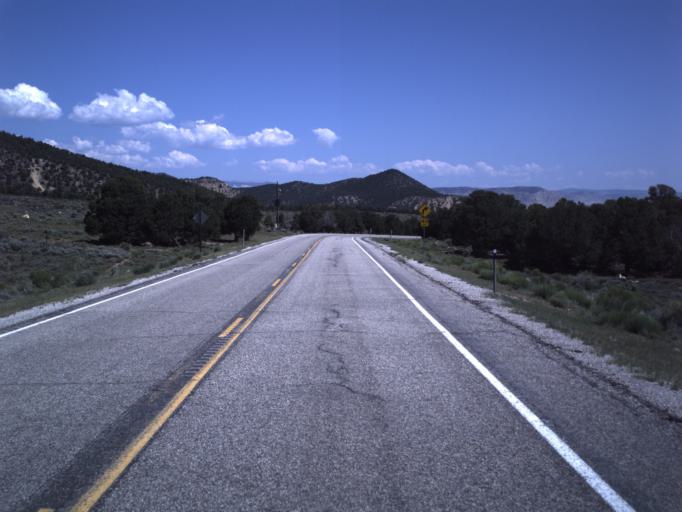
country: US
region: Utah
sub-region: Wayne County
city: Loa
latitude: 38.7112
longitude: -111.4034
